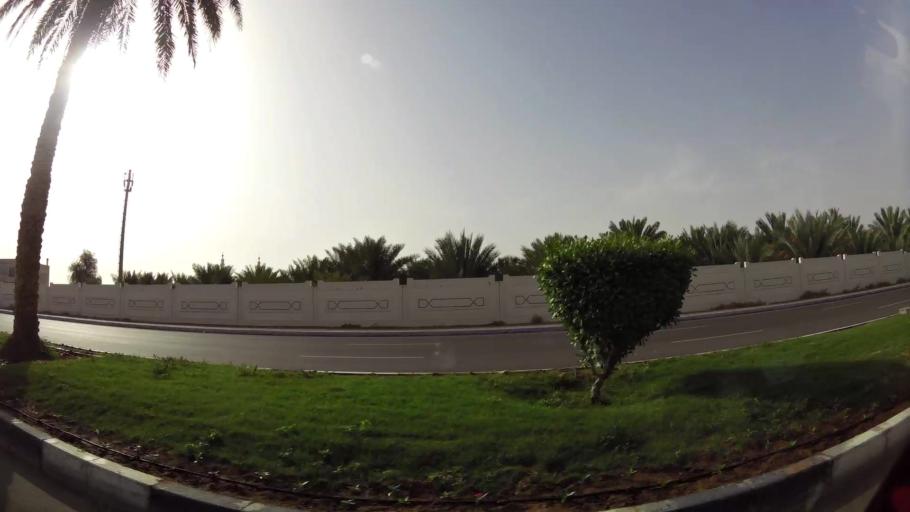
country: AE
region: Abu Dhabi
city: Al Ain
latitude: 24.1293
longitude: 55.6809
